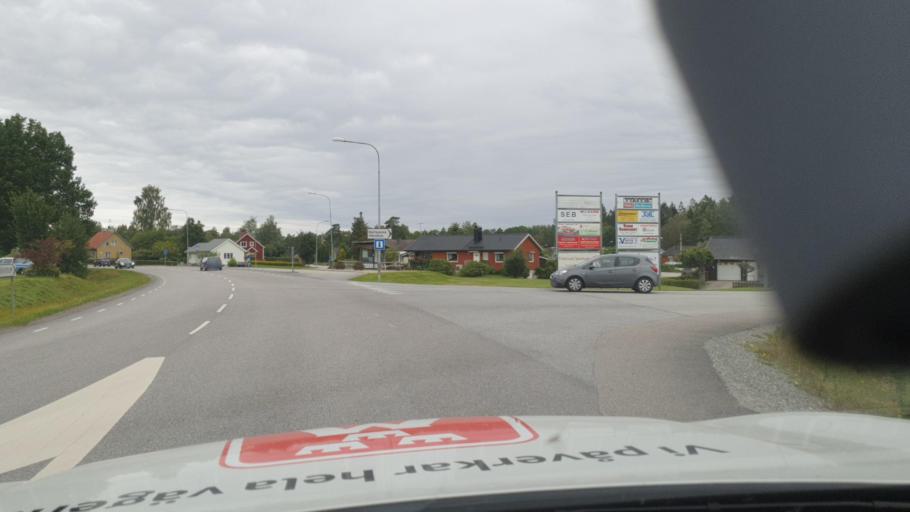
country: SE
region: Vaestra Goetaland
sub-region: Dals-Ed Kommun
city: Ed
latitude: 58.9019
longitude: 11.9444
